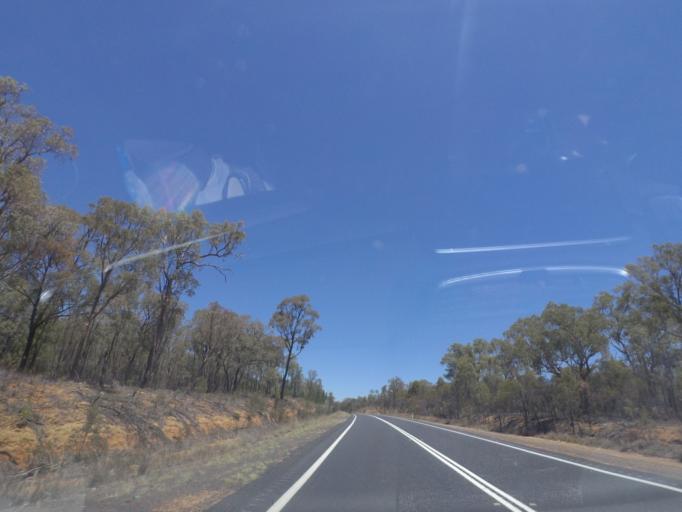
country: AU
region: New South Wales
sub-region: Warrumbungle Shire
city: Coonabarabran
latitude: -31.1792
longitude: 149.3561
